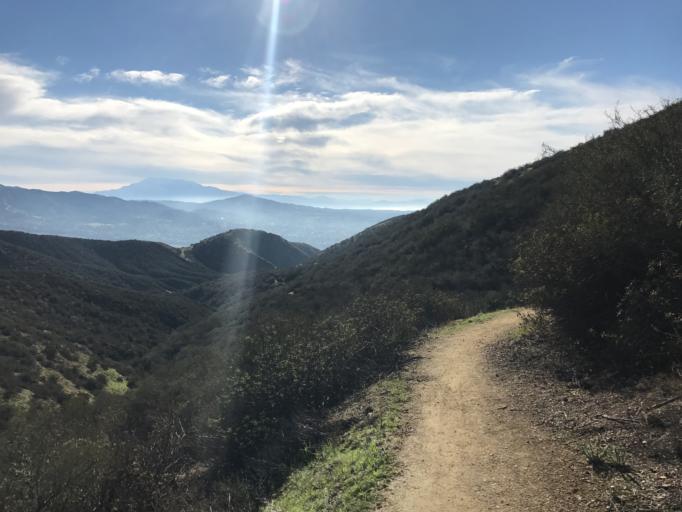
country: US
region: California
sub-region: San Bernardino County
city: Yucaipa
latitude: 34.0608
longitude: -117.0658
